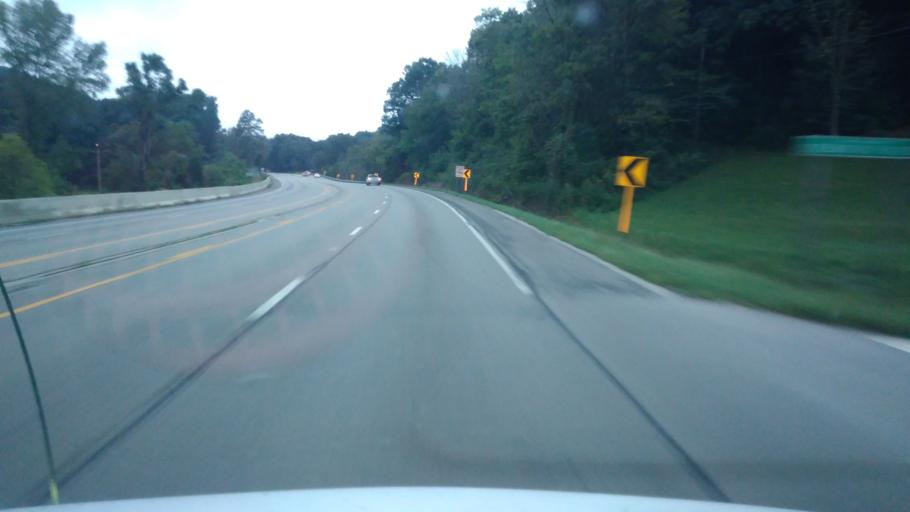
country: US
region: Ohio
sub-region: Pike County
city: Waverly
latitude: 39.2223
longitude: -82.9839
